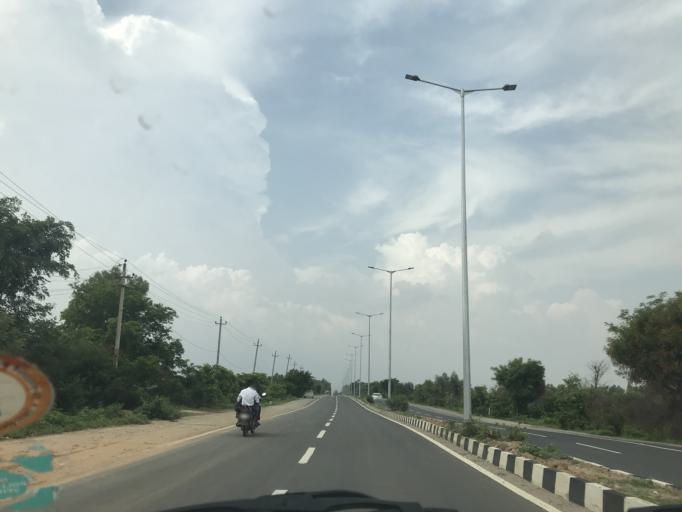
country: IN
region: Karnataka
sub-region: Bangalore Rural
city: Devanhalli
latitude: 13.1565
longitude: 77.6813
